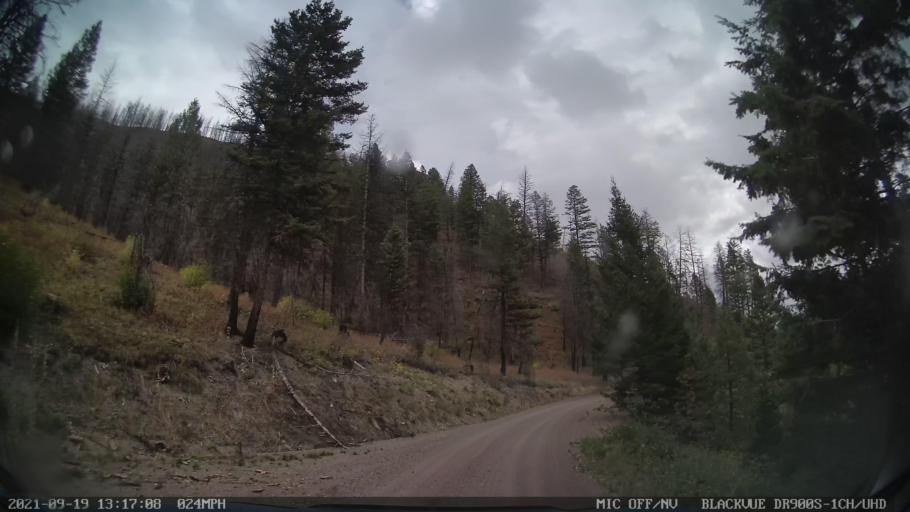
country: US
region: Montana
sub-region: Missoula County
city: Seeley Lake
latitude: 47.1759
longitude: -113.3646
